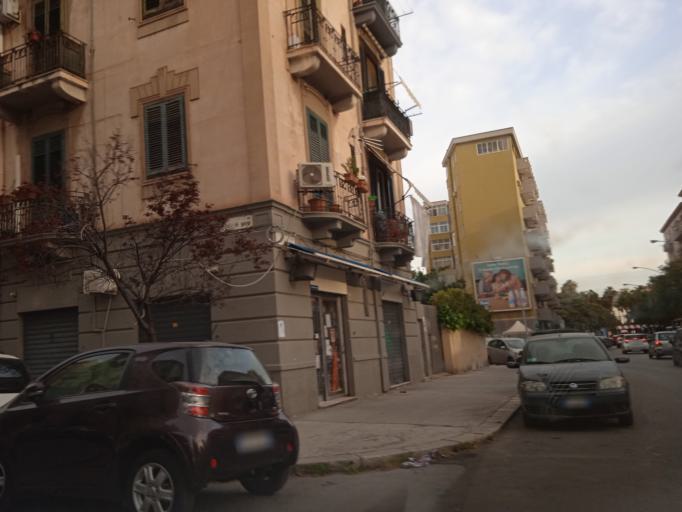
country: IT
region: Sicily
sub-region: Palermo
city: Palermo
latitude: 38.1217
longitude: 13.3471
